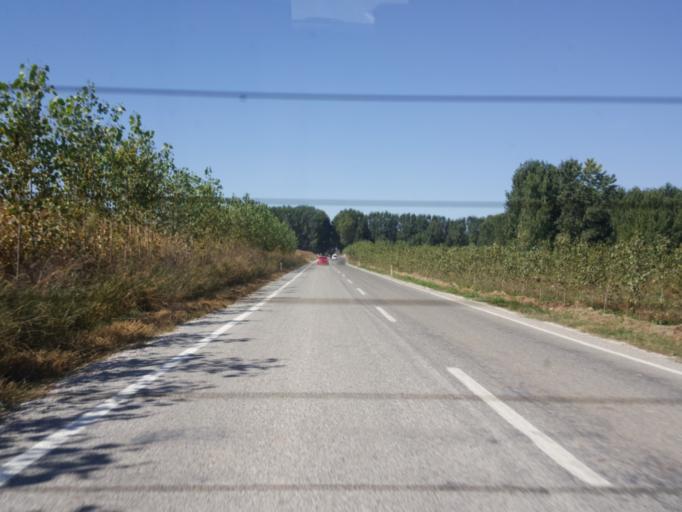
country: TR
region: Tokat
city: Pazar
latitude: 40.2679
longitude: 36.1994
